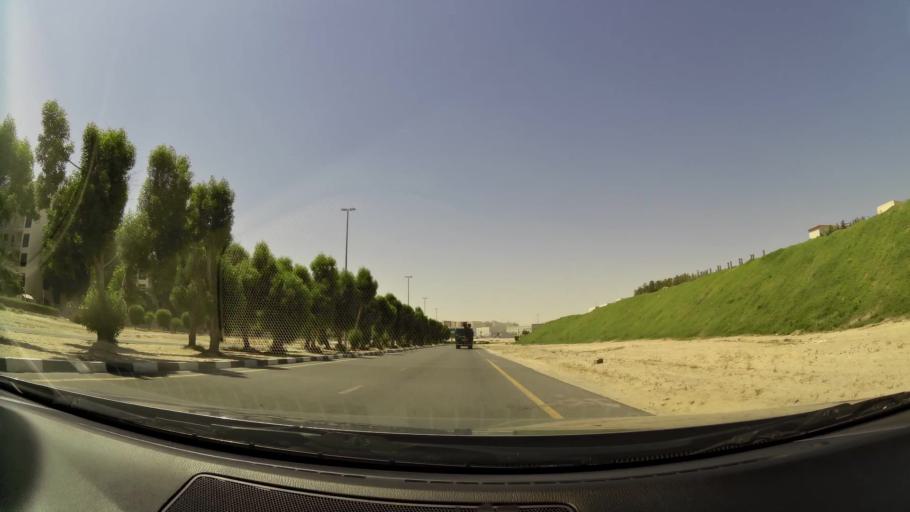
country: AE
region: Dubai
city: Dubai
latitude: 24.9866
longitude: 55.2001
